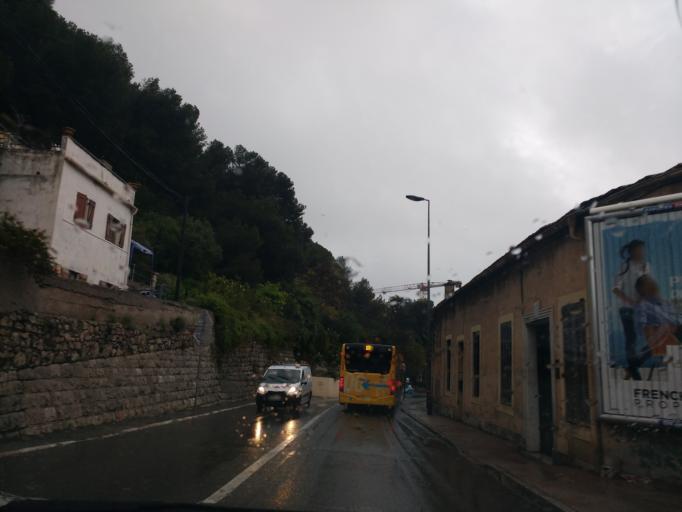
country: FR
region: Provence-Alpes-Cote d'Azur
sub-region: Departement des Alpes-Maritimes
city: Cap-d'Ail
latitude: 43.7222
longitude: 7.4013
